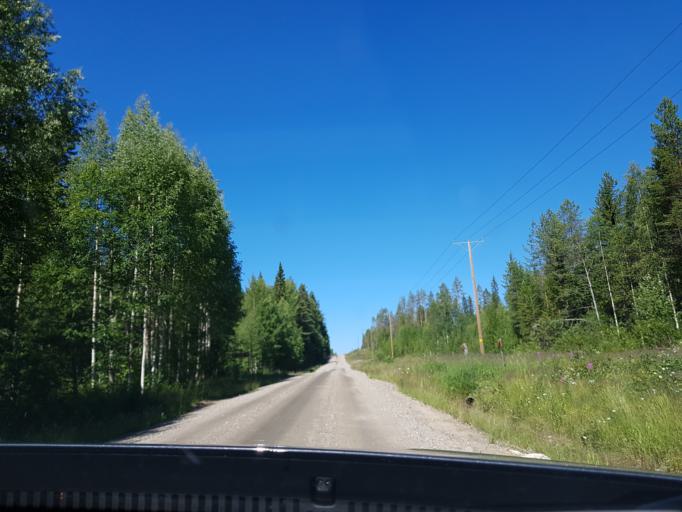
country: FI
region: Kainuu
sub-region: Kehys-Kainuu
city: Kuhmo
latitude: 64.1688
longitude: 29.6476
